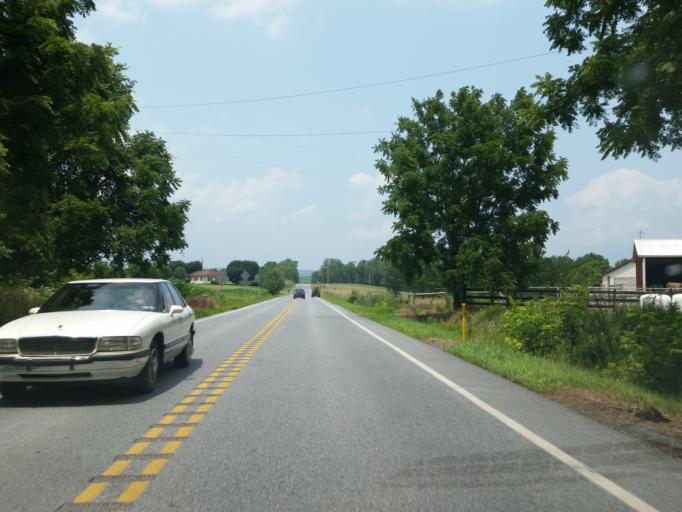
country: US
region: Pennsylvania
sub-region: Lebanon County
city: Palmyra
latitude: 40.3543
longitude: -76.6170
